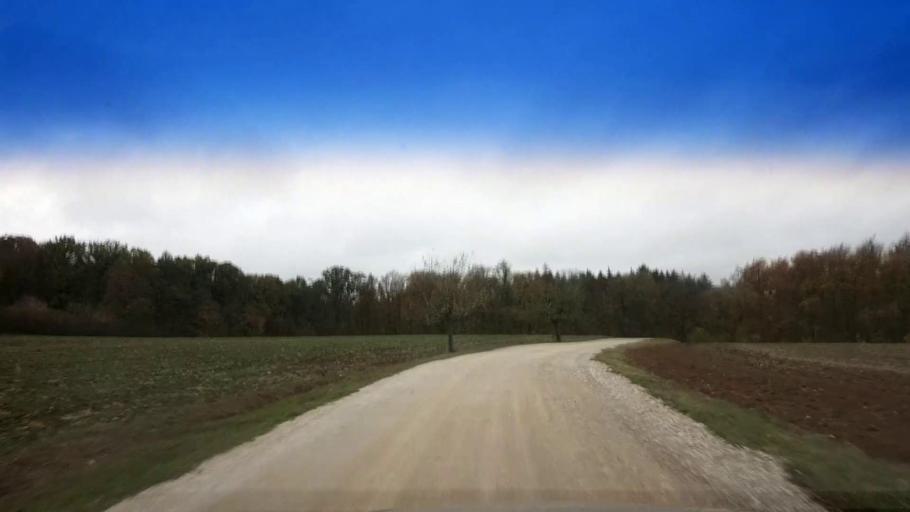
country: DE
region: Bavaria
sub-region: Upper Franconia
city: Schesslitz
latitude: 49.9661
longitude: 11.0320
